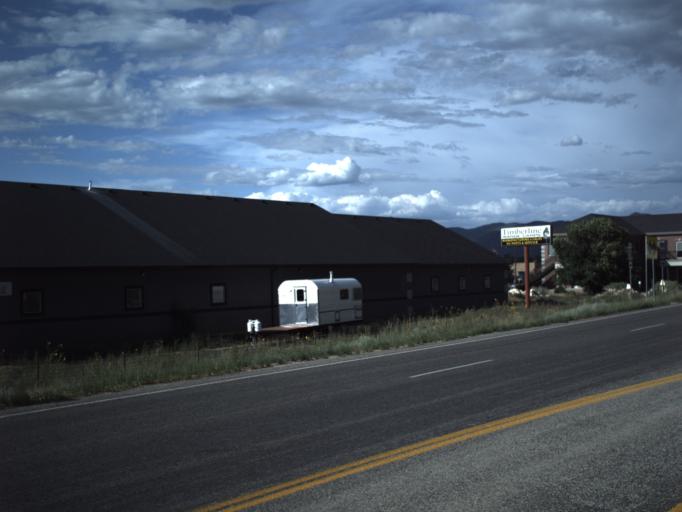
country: US
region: Utah
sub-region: Sanpete County
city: Mount Pleasant
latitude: 39.5290
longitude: -111.4676
